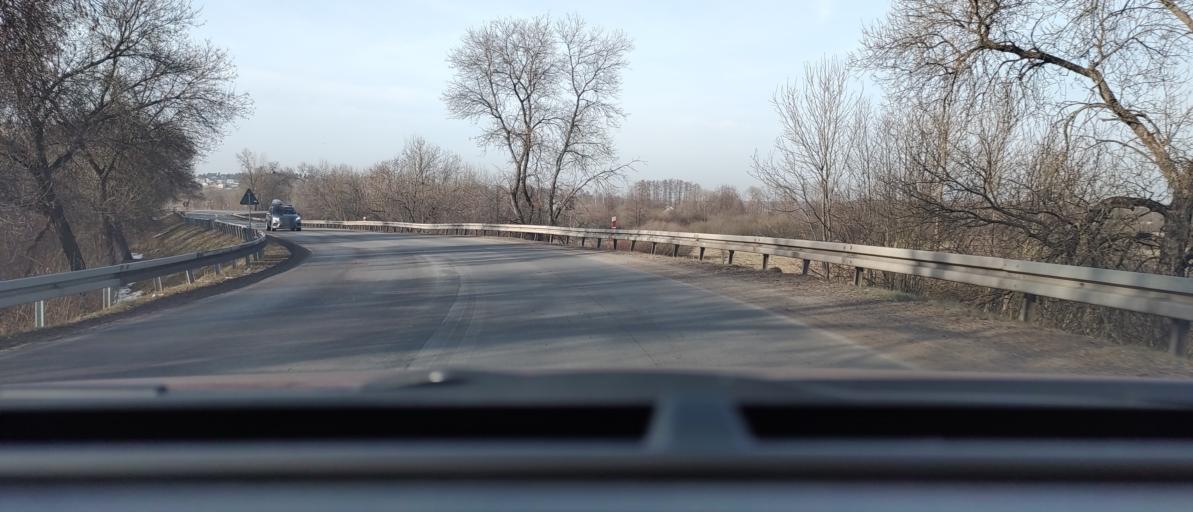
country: PL
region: Masovian Voivodeship
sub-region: Powiat bialobrzeski
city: Bialobrzegi
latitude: 51.6600
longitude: 20.9532
